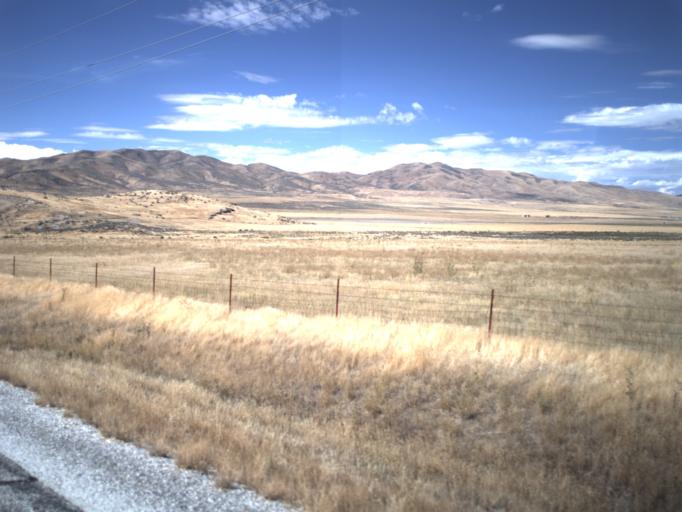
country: US
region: Utah
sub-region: Box Elder County
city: Tremonton
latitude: 41.7224
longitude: -112.4379
